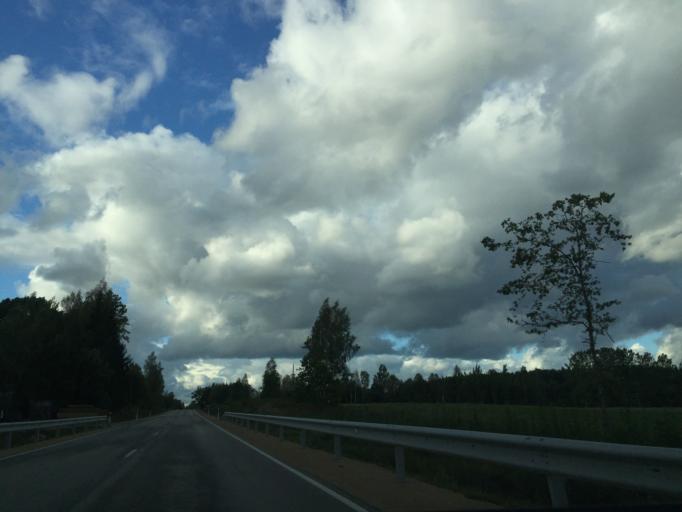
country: LV
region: Ligatne
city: Ligatne
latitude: 57.1693
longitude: 25.0456
